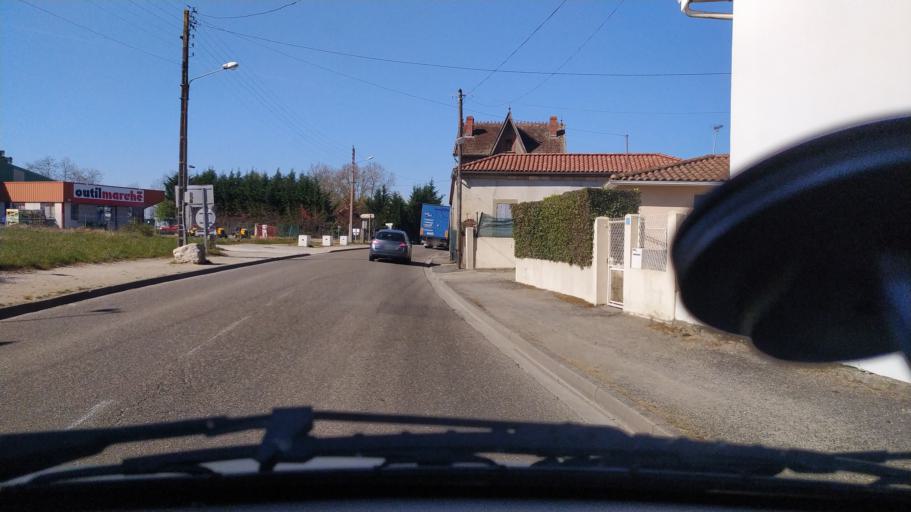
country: FR
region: Midi-Pyrenees
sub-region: Departement du Gers
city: Nogaro
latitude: 43.7642
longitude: -0.0316
